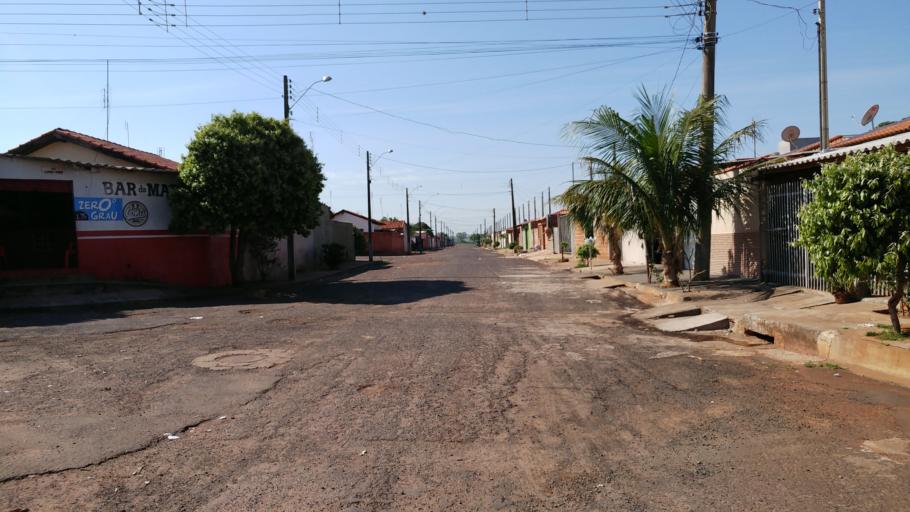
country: BR
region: Sao Paulo
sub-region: Paraguacu Paulista
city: Paraguacu Paulista
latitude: -22.4100
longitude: -50.5633
